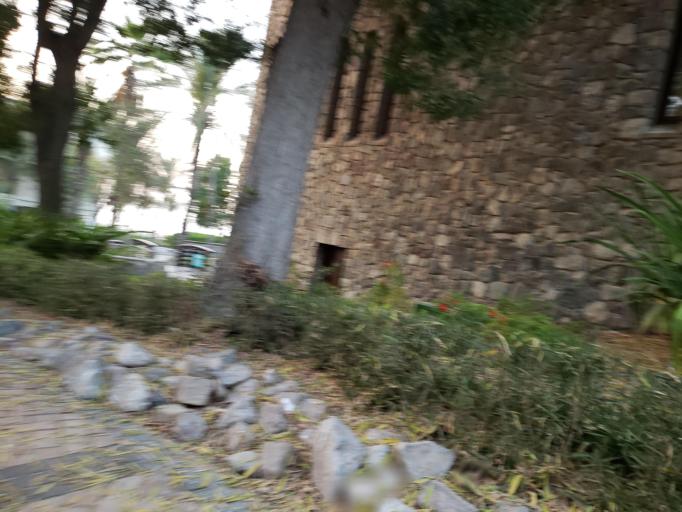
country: AE
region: Dubai
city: Dubai
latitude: 24.9874
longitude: 55.0216
